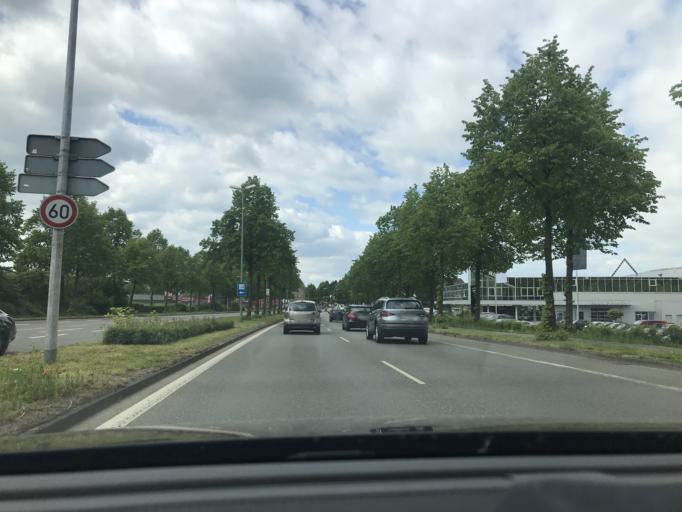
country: DE
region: North Rhine-Westphalia
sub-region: Regierungsbezirk Munster
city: Bottrop
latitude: 51.5429
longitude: 6.9190
